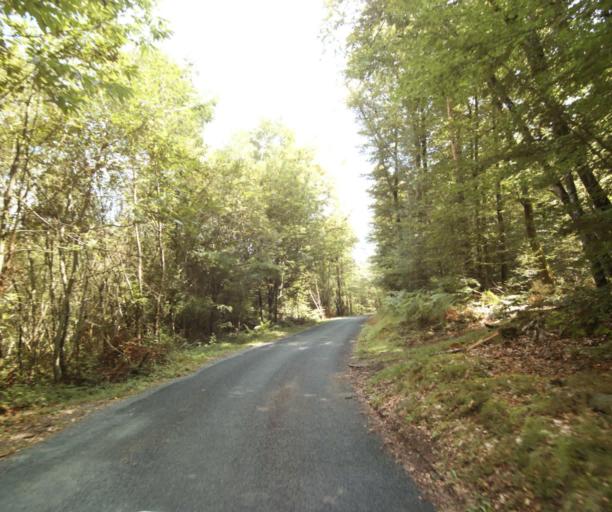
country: FR
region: Limousin
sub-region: Departement de la Correze
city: Sainte-Fortunade
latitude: 45.2095
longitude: 1.8218
